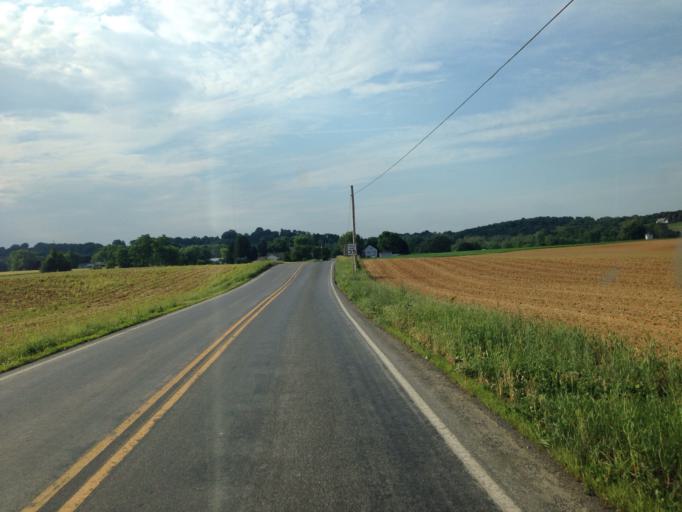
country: US
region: Pennsylvania
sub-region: Lancaster County
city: Rothsville
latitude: 40.1281
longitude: -76.2590
